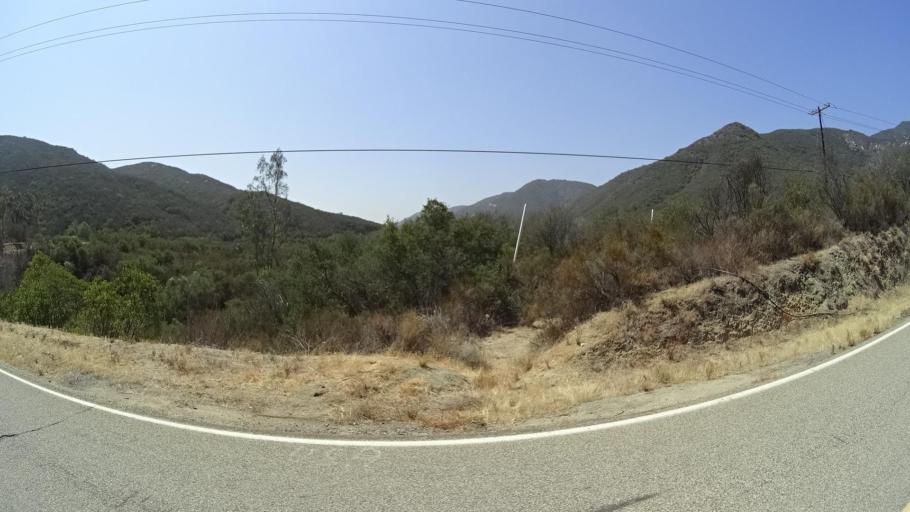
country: US
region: California
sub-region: San Diego County
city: Fallbrook
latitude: 33.4170
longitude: -117.3190
